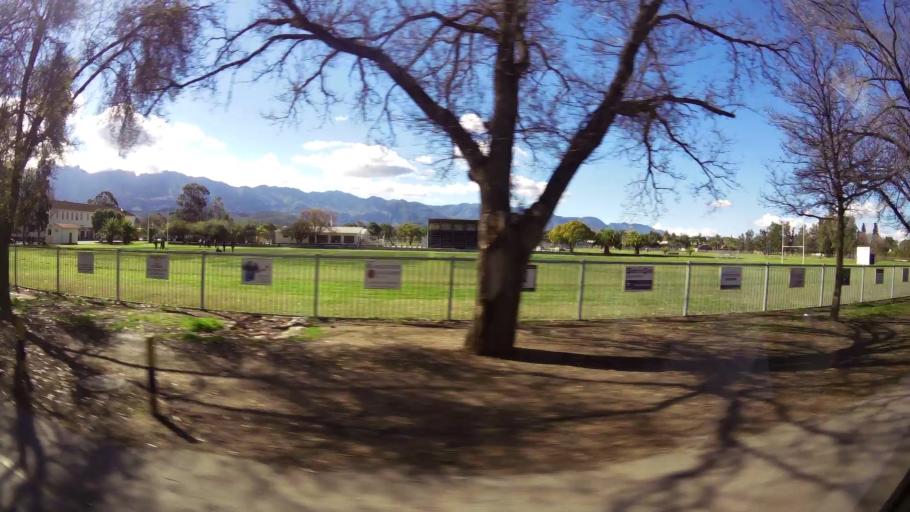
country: ZA
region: Western Cape
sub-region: Cape Winelands District Municipality
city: Ashton
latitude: -33.8091
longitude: 19.8877
